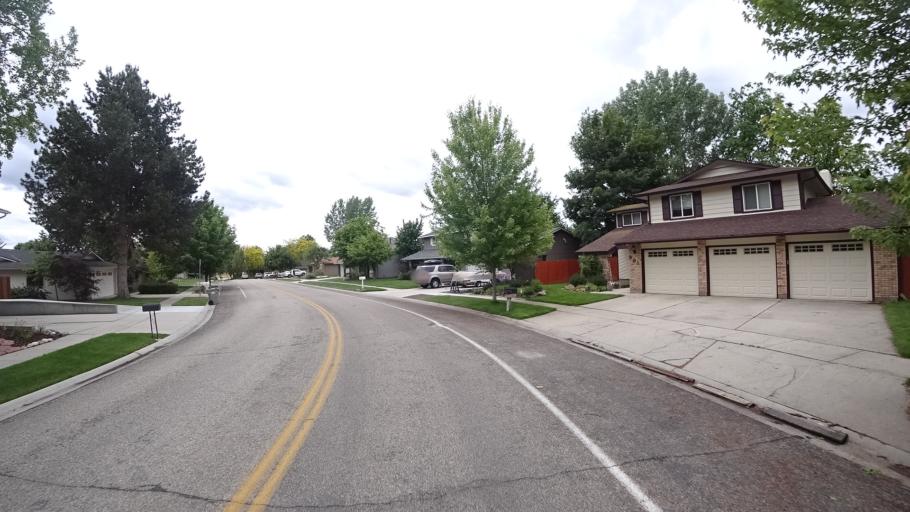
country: US
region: Idaho
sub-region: Ada County
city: Eagle
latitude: 43.7038
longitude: -116.3433
